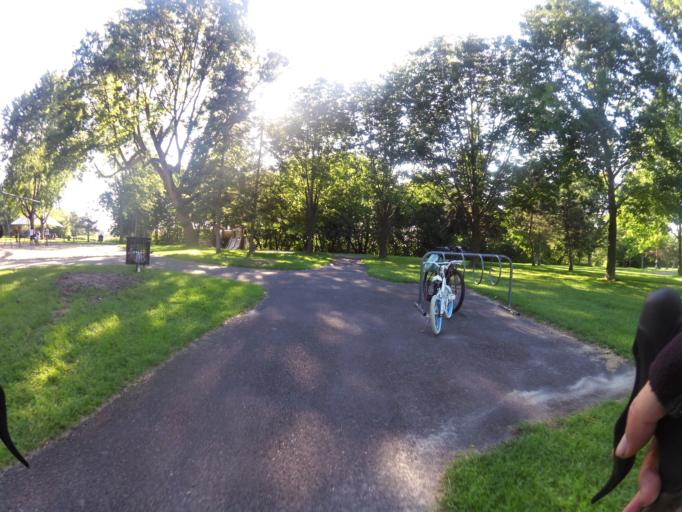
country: CA
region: Ontario
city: Ottawa
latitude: 45.2731
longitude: -75.6988
